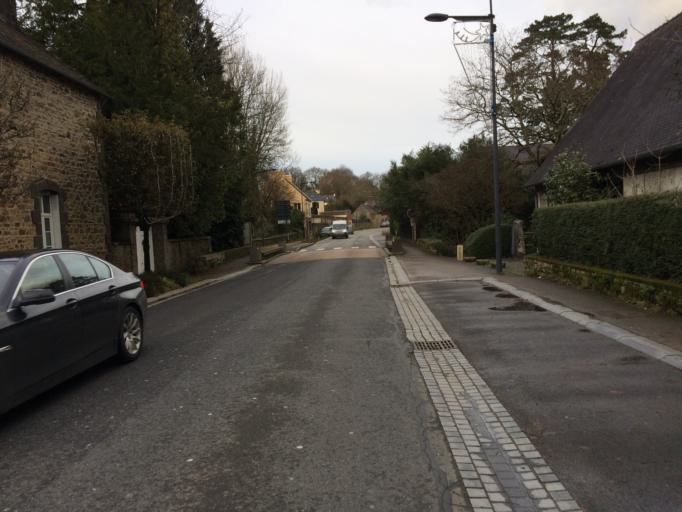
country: FR
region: Brittany
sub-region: Departement du Finistere
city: Daoulas
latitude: 48.3626
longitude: -4.2596
